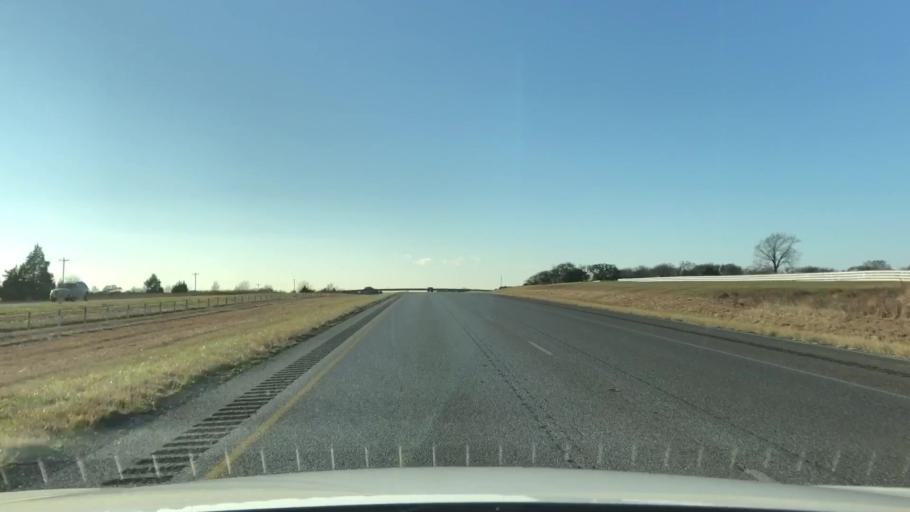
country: US
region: Texas
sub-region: Fayette County
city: Schulenburg
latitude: 29.6892
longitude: -96.9597
